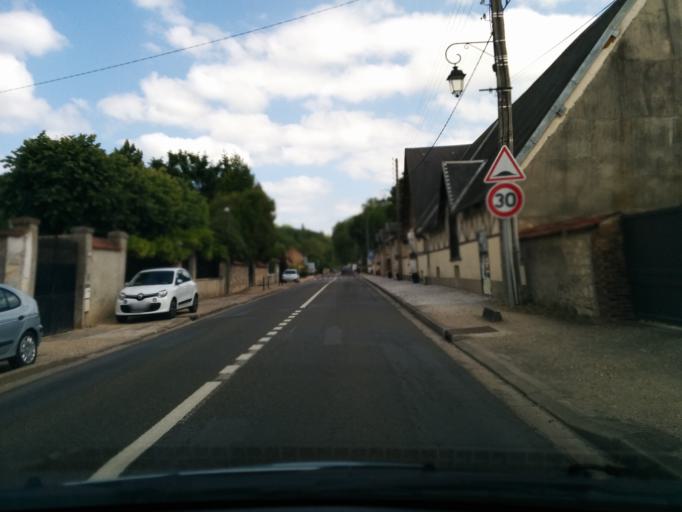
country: FR
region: Ile-de-France
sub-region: Departement des Yvelines
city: Maule
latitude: 48.9084
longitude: 1.8578
